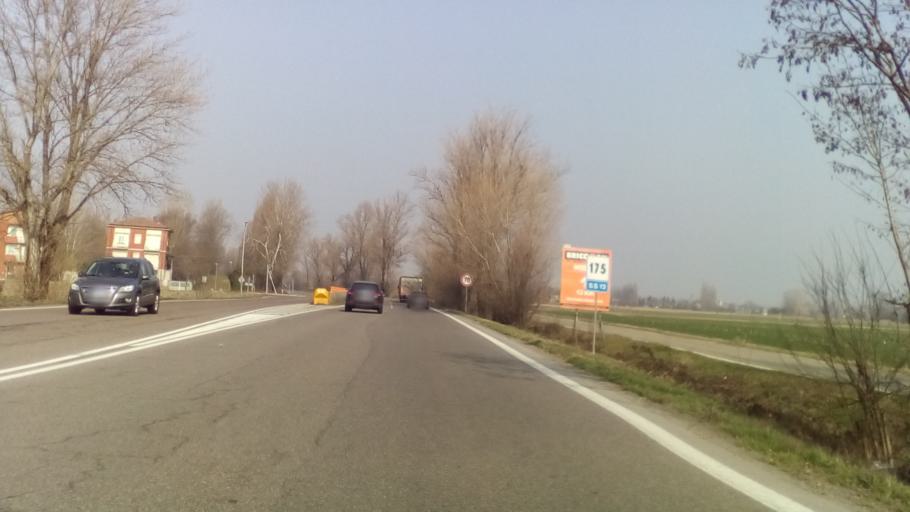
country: IT
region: Emilia-Romagna
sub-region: Provincia di Modena
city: Modena
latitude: 44.6164
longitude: 10.9397
